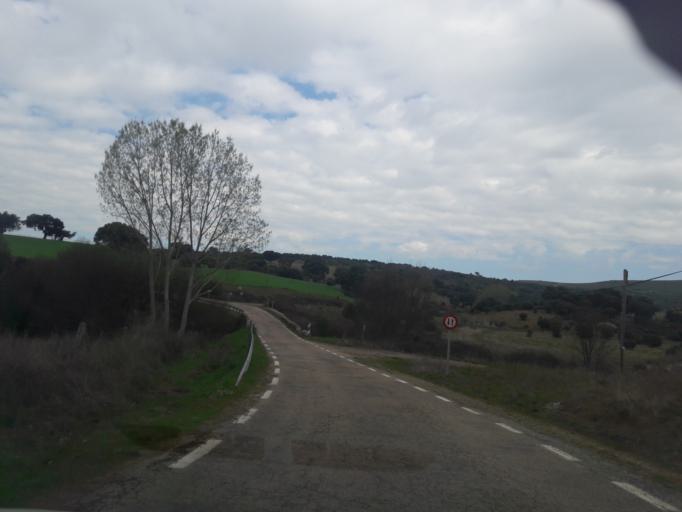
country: ES
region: Castille and Leon
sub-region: Provincia de Salamanca
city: Serradilla del Arroyo
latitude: 40.5221
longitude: -6.3725
